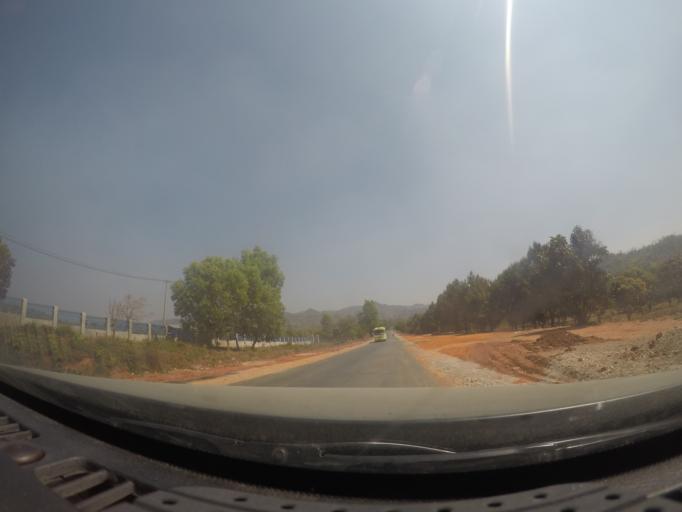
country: MM
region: Shan
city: Taunggyi
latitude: 20.8102
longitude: 97.2325
